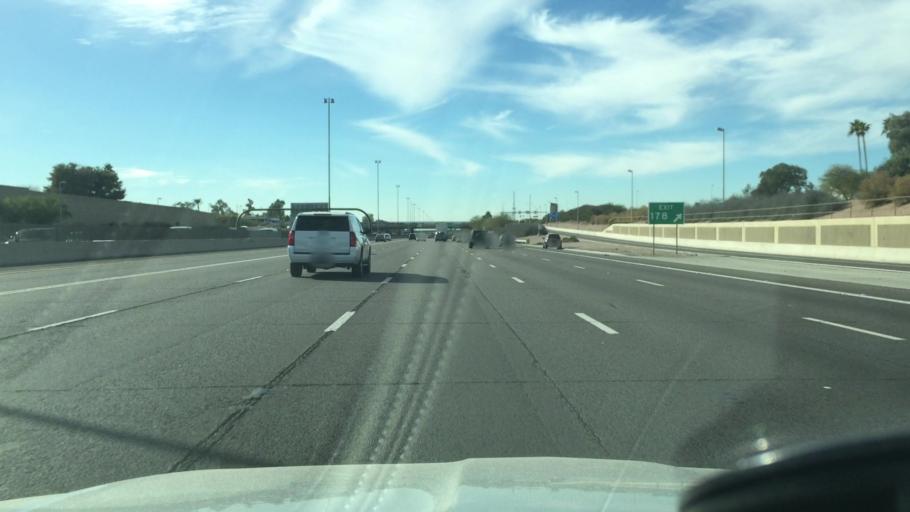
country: US
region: Arizona
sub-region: Maricopa County
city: San Carlos
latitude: 33.3864
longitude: -111.8523
